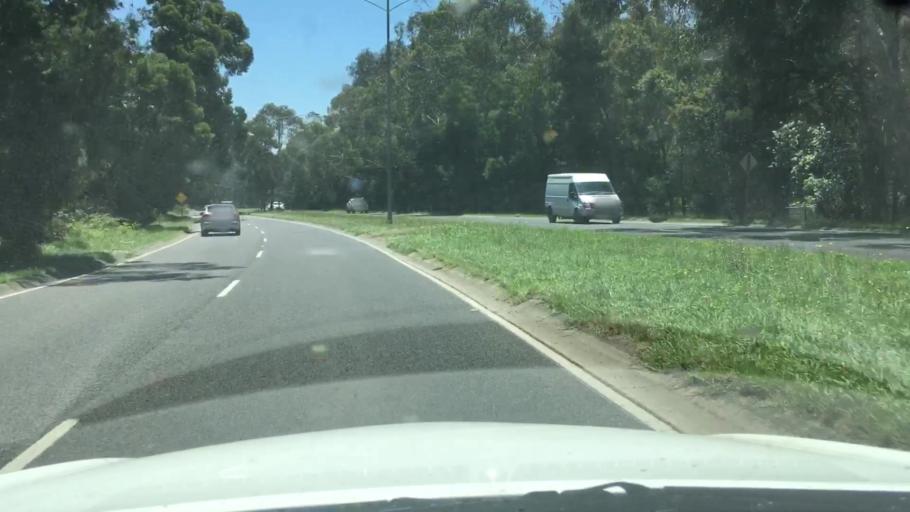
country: AU
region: Victoria
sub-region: Yarra Ranges
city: Kalorama
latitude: -37.8007
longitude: 145.3586
